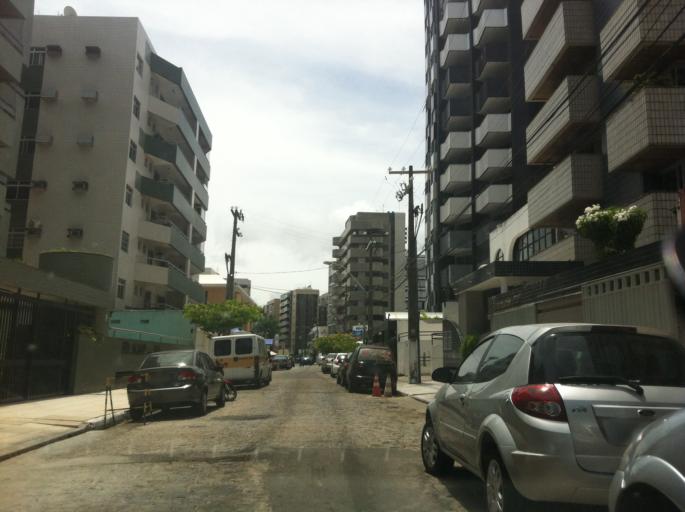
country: BR
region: Alagoas
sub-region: Maceio
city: Maceio
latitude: -9.6627
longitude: -35.7033
